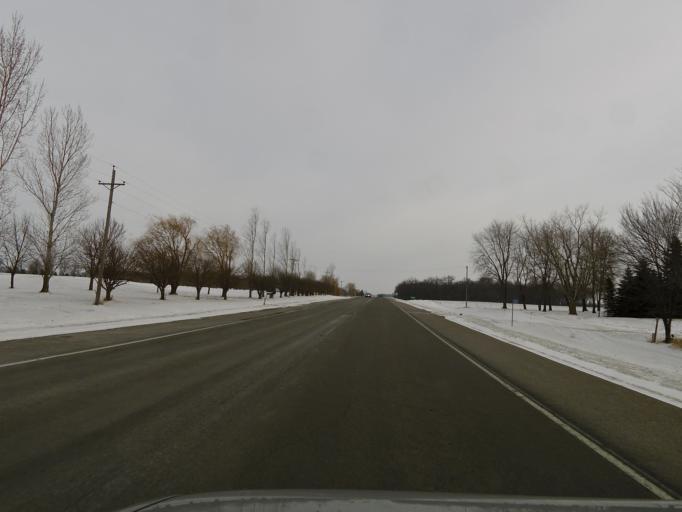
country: US
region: Minnesota
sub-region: McLeod County
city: Lester Prairie
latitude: 44.9063
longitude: -94.0633
